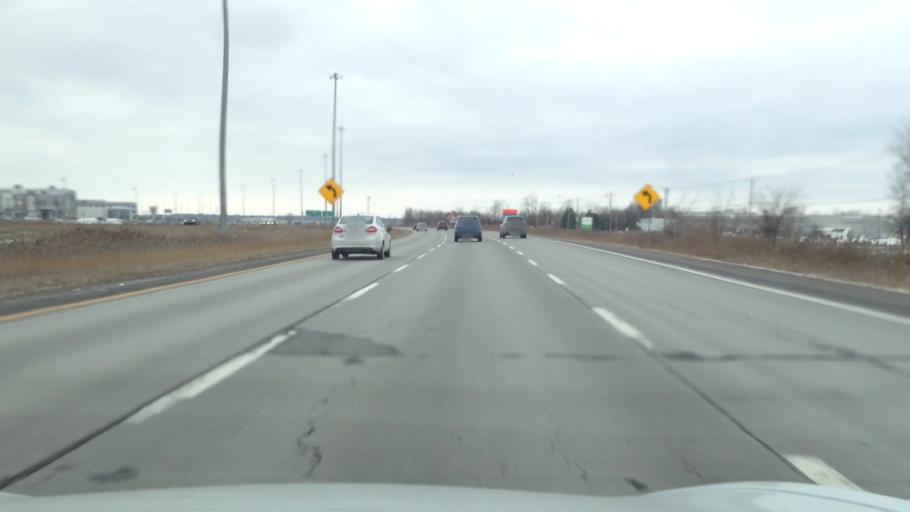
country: CA
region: Quebec
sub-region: Monteregie
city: Vaudreuil-Dorion
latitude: 45.4160
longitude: -74.0224
